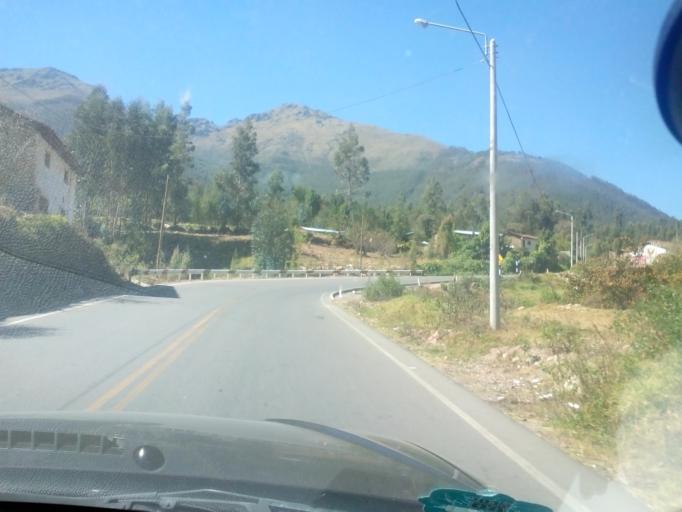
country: PE
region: Apurimac
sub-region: Chincheros
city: Chincheros
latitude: -13.5153
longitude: -73.7070
